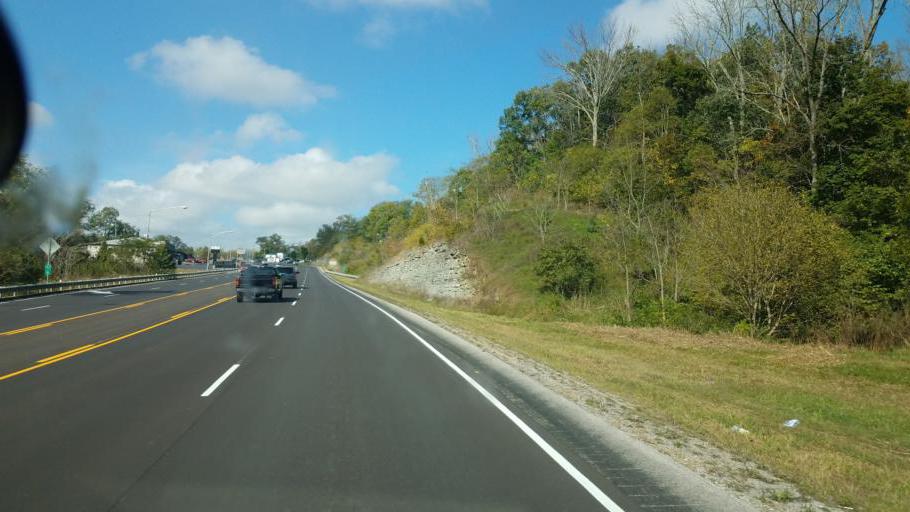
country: US
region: Ohio
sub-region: Brown County
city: Aberdeen
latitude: 38.6431
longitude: -83.7727
